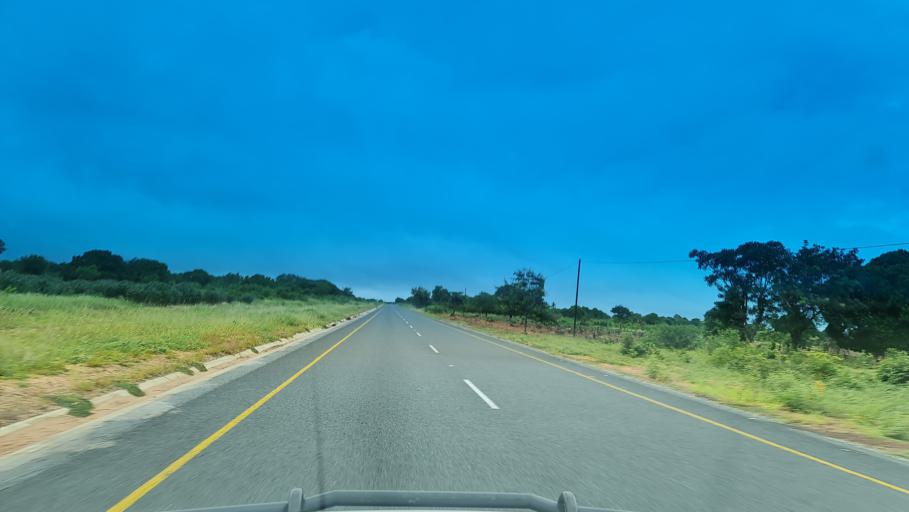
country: MZ
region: Nampula
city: Nampula
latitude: -15.5875
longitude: 39.3247
